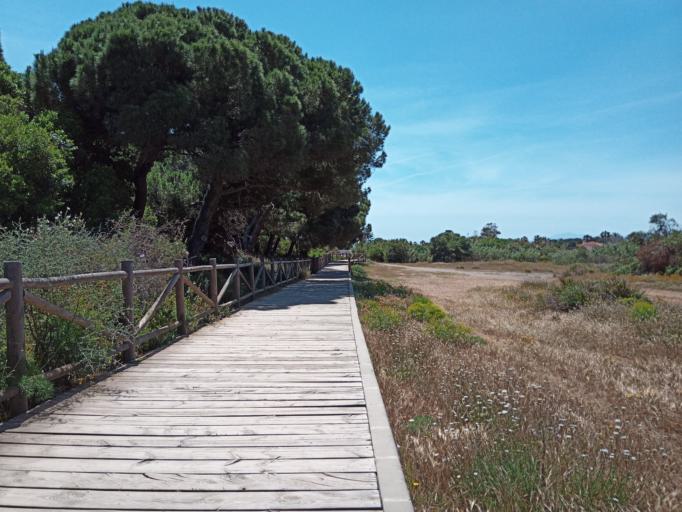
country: ES
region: Andalusia
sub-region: Provincia de Malaga
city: Ojen
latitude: 36.4869
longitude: -4.7513
